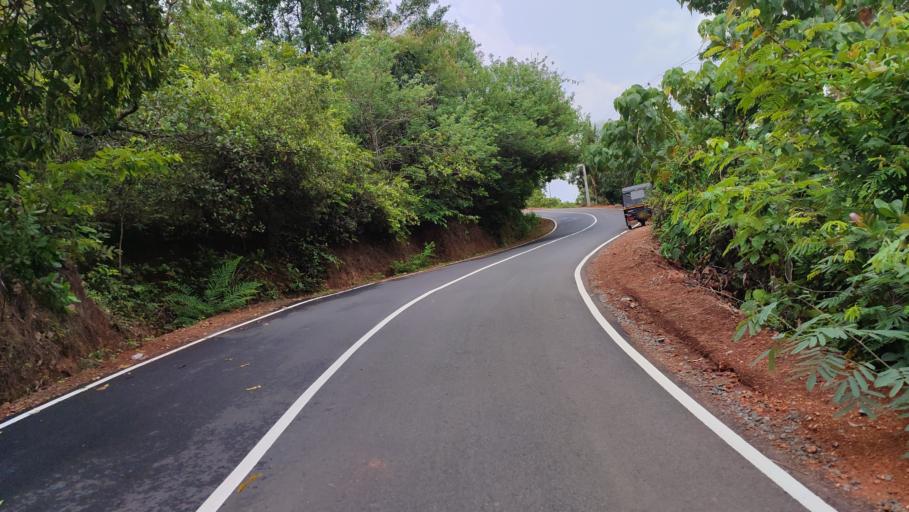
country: IN
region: Kerala
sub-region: Kasaragod District
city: Kannangad
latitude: 12.3196
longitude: 75.1515
